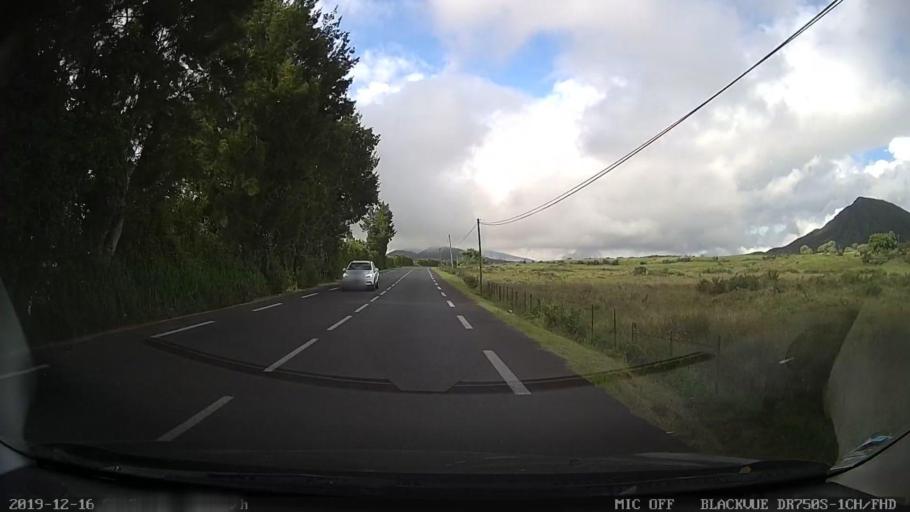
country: RE
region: Reunion
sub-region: Reunion
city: Le Tampon
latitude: -21.1842
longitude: 55.5796
